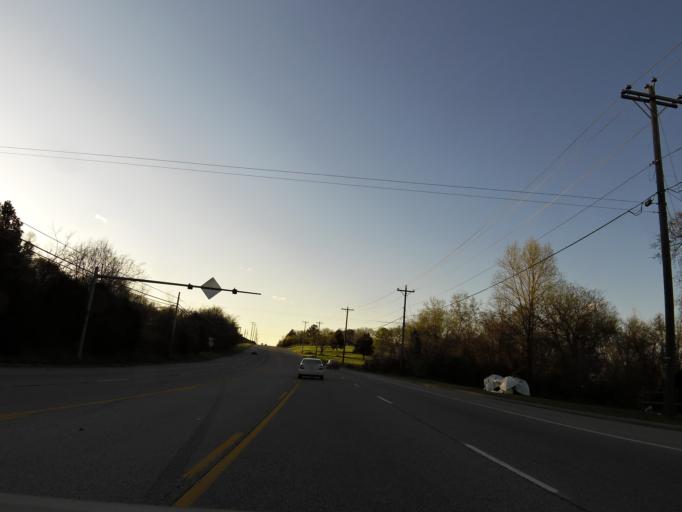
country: US
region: Tennessee
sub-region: Sumner County
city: Millersville
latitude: 36.3593
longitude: -86.7261
